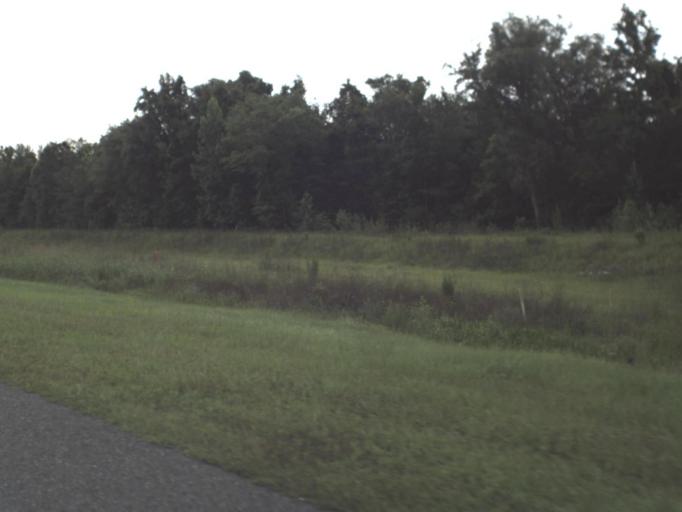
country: US
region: Florida
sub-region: Levy County
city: Inglis
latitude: 29.1883
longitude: -82.6831
